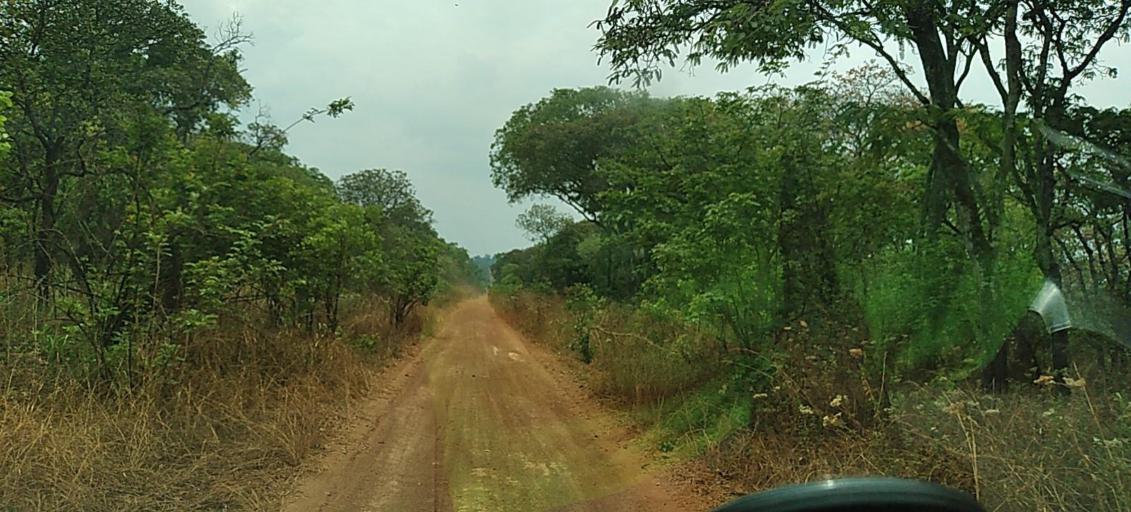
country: ZM
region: North-Western
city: Kansanshi
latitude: -12.0346
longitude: 26.3180
